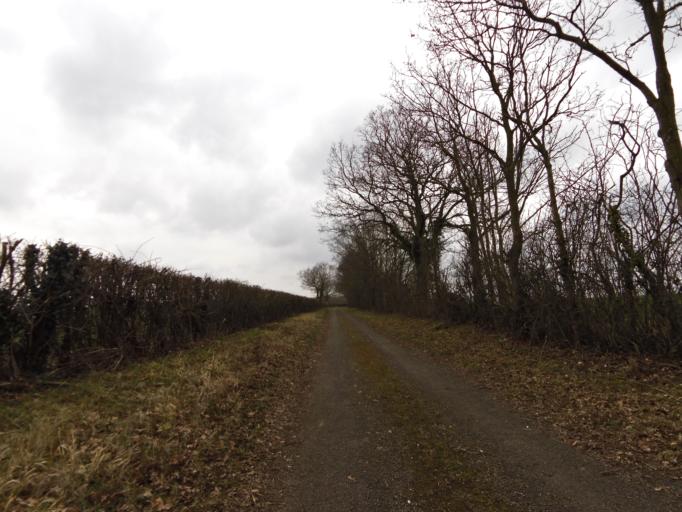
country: GB
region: England
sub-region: Suffolk
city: Halesworth
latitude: 52.3680
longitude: 1.5189
